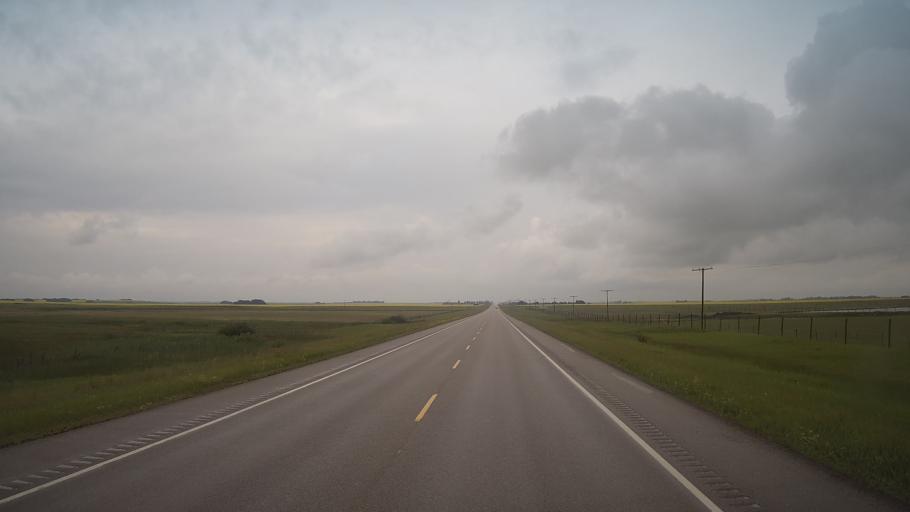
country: CA
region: Saskatchewan
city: Unity
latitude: 52.4349
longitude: -108.9902
